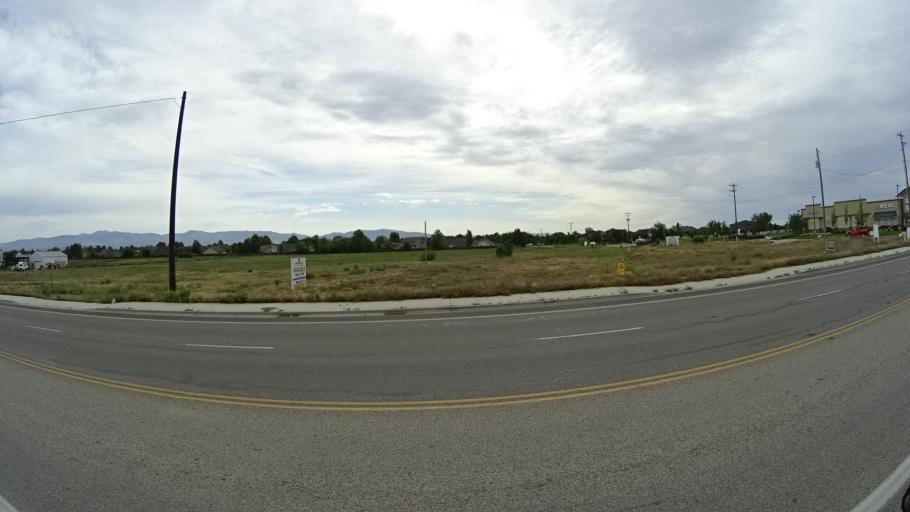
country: US
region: Idaho
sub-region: Ada County
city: Meridian
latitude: 43.5762
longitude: -116.3545
